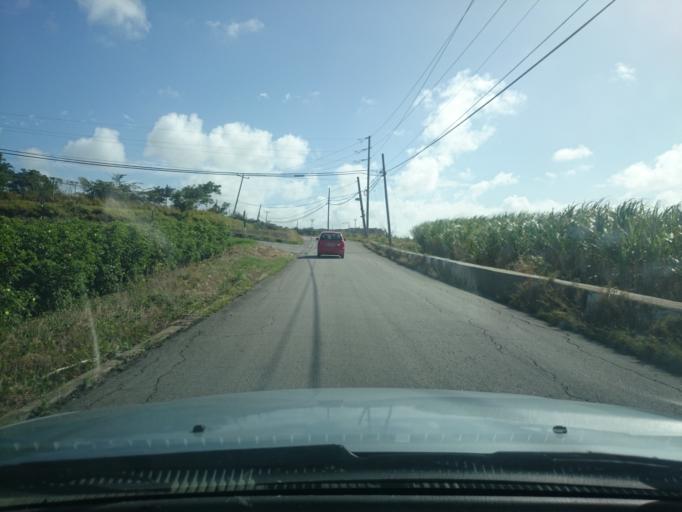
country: BB
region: Saint Lucy
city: Checker Hall
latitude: 13.3017
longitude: -59.6166
